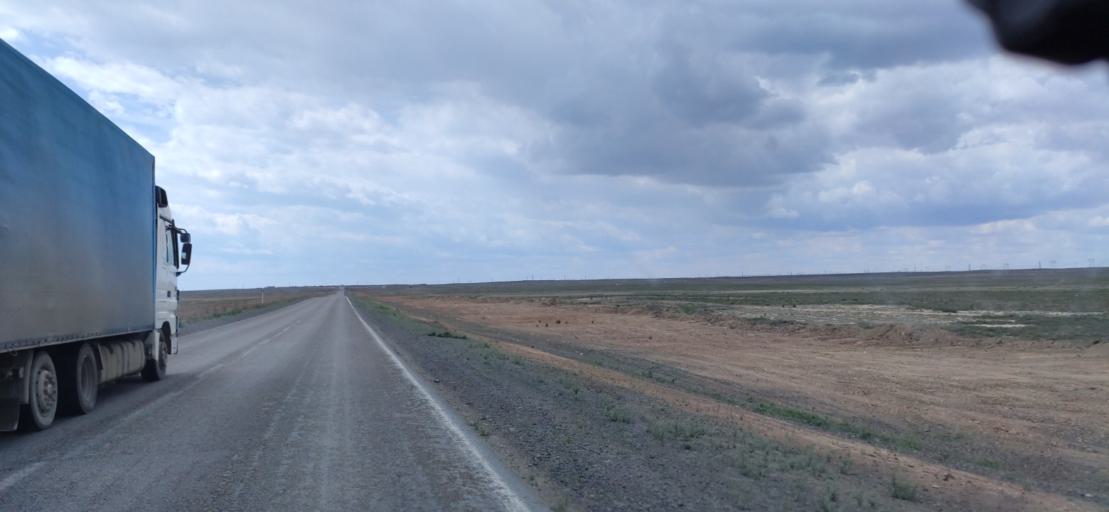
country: KZ
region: Qaraghandy
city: Saryshaghan
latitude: 46.0565
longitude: 73.5979
